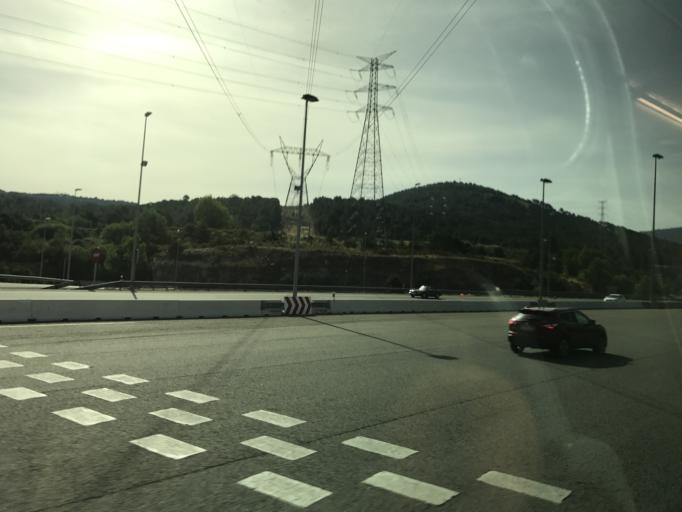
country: ES
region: Castille and Leon
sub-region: Provincia de Segovia
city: Otero de Herreros
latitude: 40.7280
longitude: -4.1936
